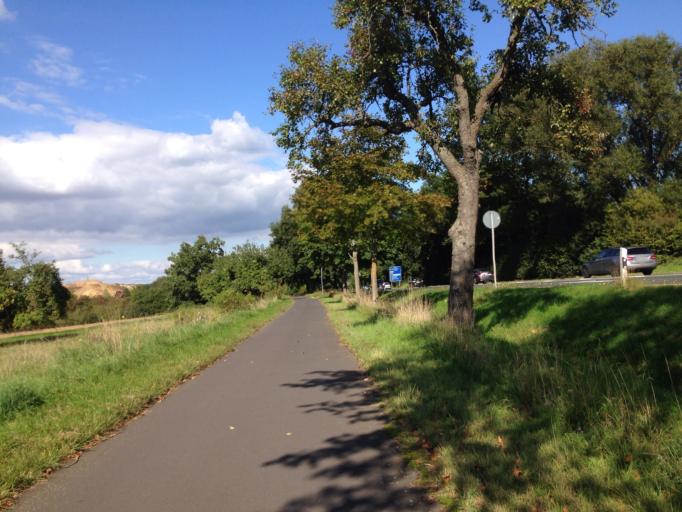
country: DE
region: Hesse
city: Lollar
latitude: 50.6180
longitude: 8.7048
